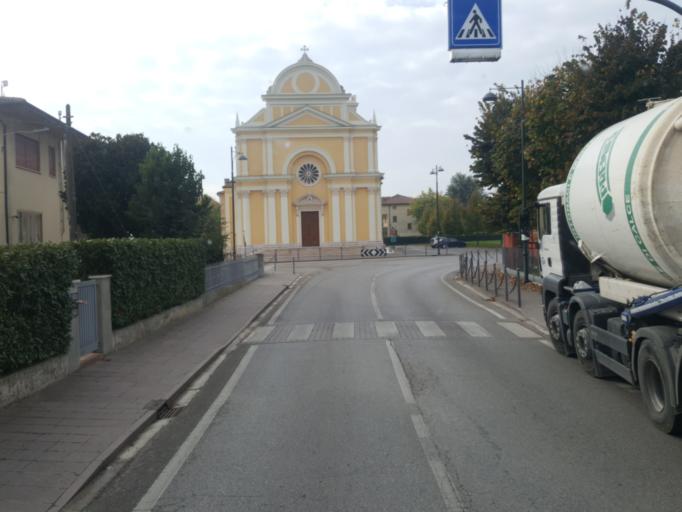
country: IT
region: Veneto
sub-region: Provincia di Treviso
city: Ca' Rainati
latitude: 45.7559
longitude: 11.8493
